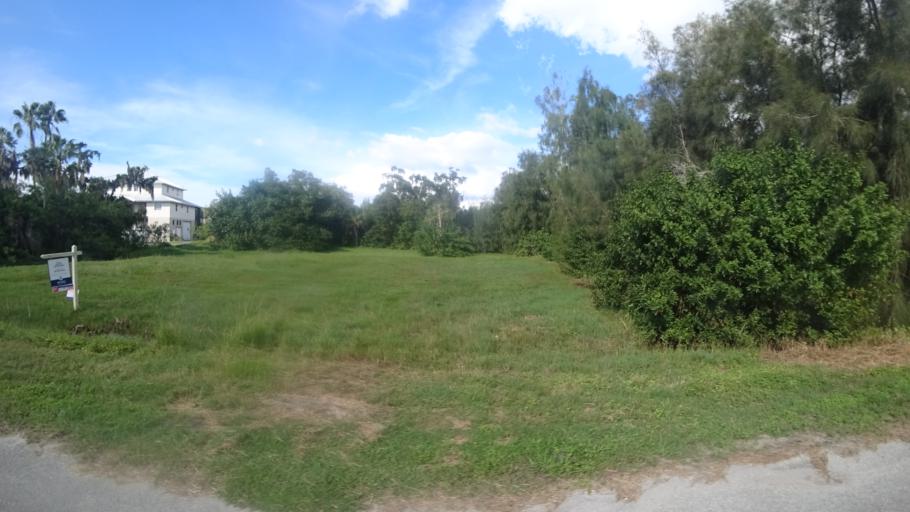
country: US
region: Florida
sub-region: Manatee County
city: Memphis
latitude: 27.5752
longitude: -82.5882
